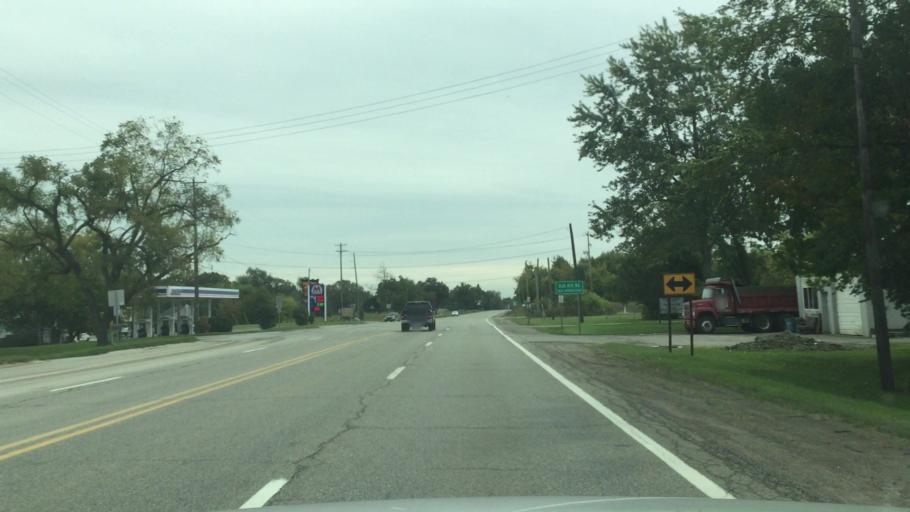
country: US
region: Michigan
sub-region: Oakland County
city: Ortonville
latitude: 42.7891
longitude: -83.5096
